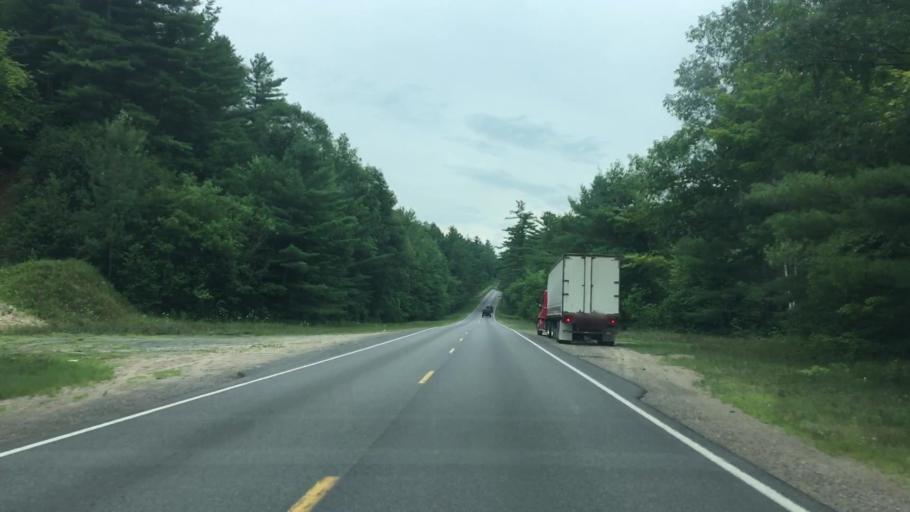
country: US
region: New York
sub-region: Clinton County
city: Peru
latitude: 44.4949
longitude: -73.5924
